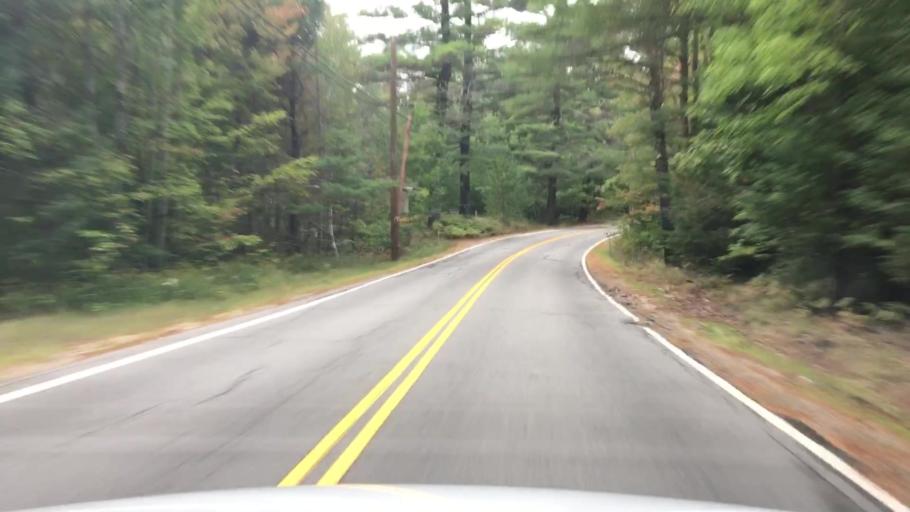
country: US
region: New Hampshire
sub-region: Carroll County
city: Effingham
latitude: 43.7203
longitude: -70.9976
